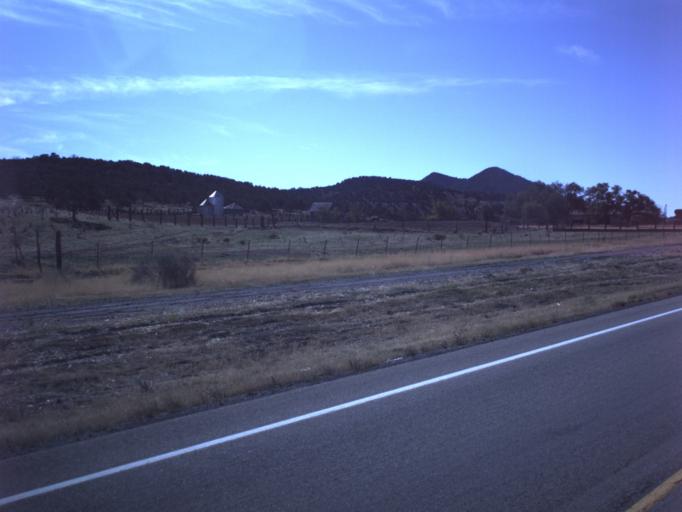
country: US
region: Utah
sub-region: Juab County
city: Nephi
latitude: 39.4454
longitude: -111.9129
